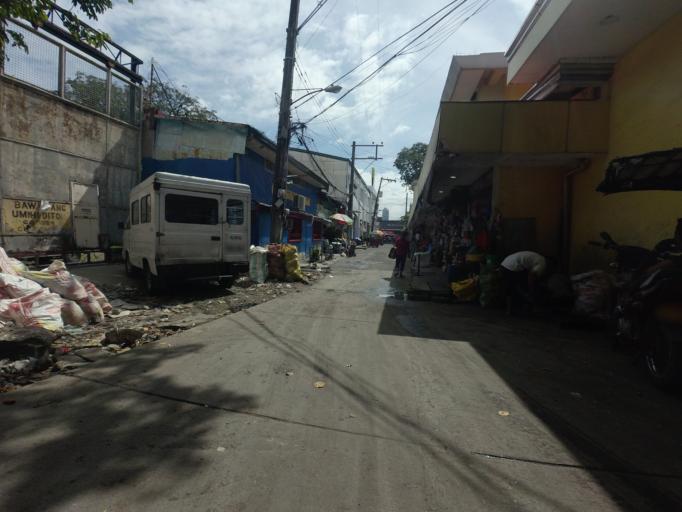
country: PH
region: Metro Manila
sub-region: San Juan
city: San Juan
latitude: 14.5823
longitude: 121.0120
